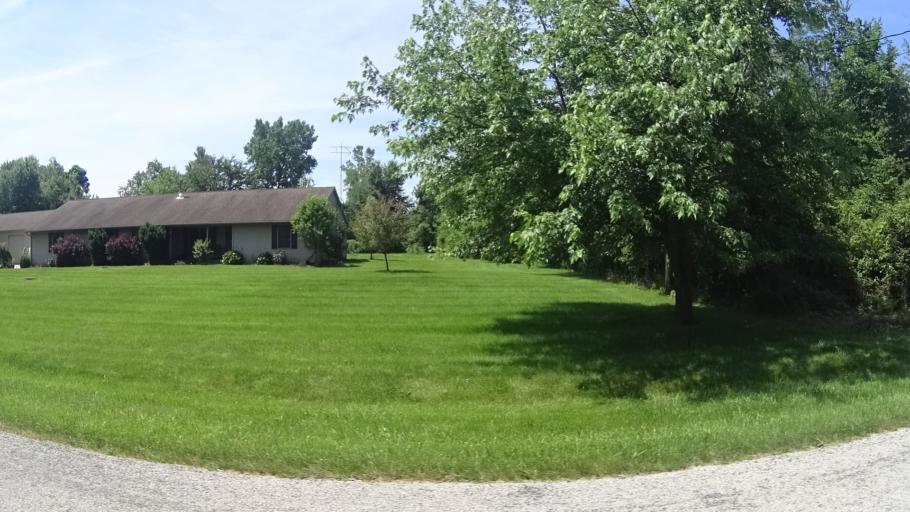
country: US
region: Ohio
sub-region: Erie County
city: Huron
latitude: 41.3568
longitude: -82.4825
